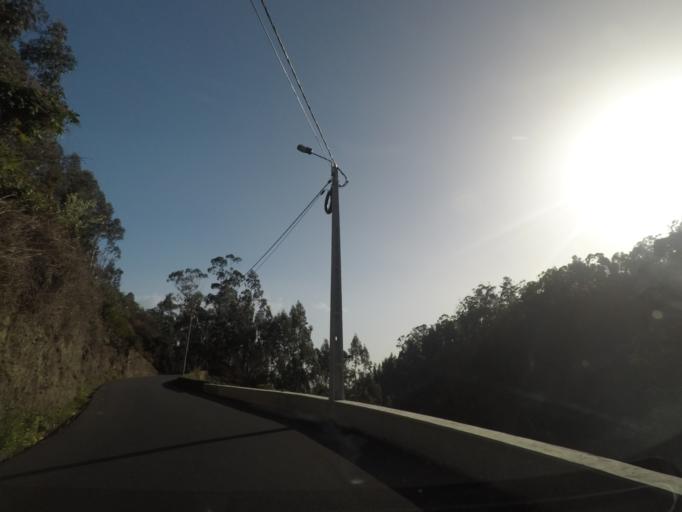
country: PT
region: Madeira
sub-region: Ribeira Brava
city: Campanario
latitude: 32.6745
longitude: -17.0045
